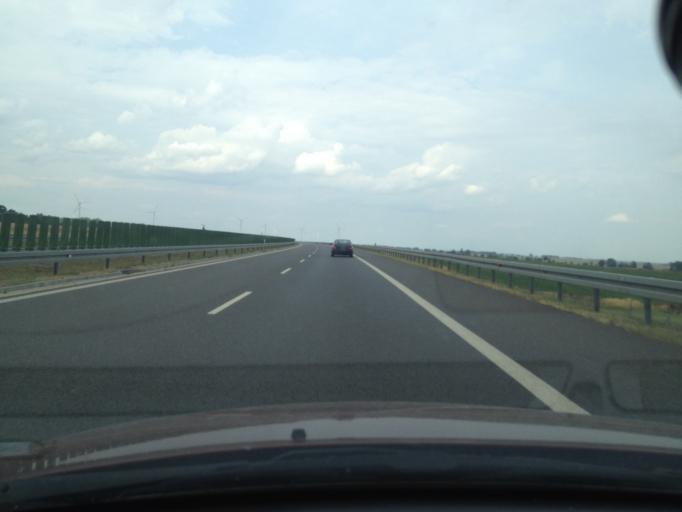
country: PL
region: West Pomeranian Voivodeship
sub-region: Powiat pyrzycki
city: Kozielice
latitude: 53.0700
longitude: 14.8614
